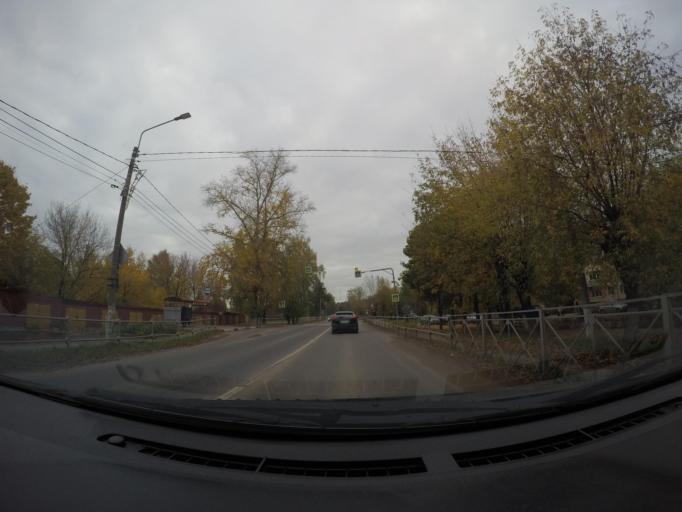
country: RU
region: Moskovskaya
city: Elektrougli
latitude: 55.7676
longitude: 38.2190
